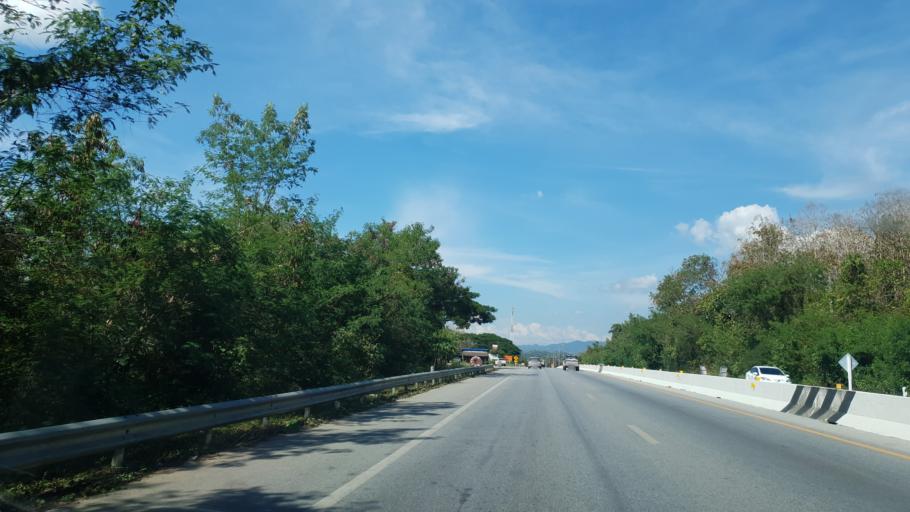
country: TH
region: Uttaradit
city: Uttaradit
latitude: 17.7239
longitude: 100.1343
